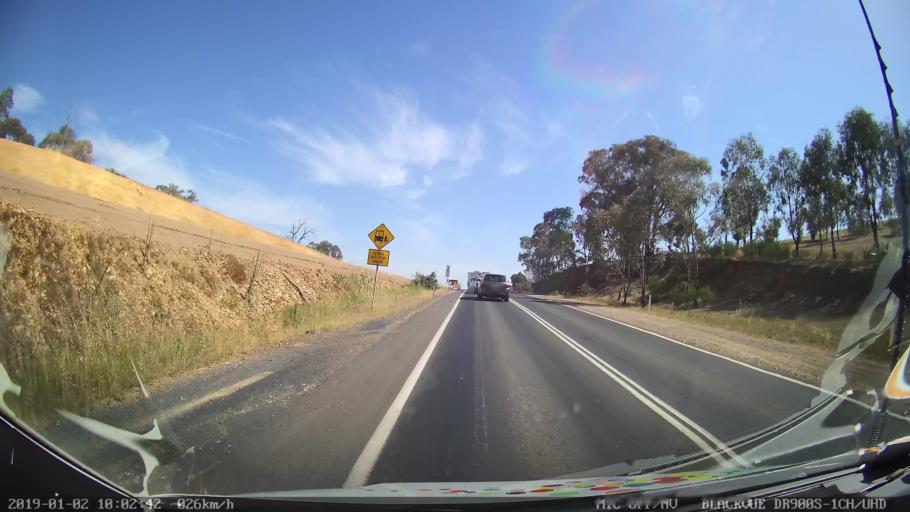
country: AU
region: New South Wales
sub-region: Gundagai
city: Gundagai
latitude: -35.1821
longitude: 148.1263
